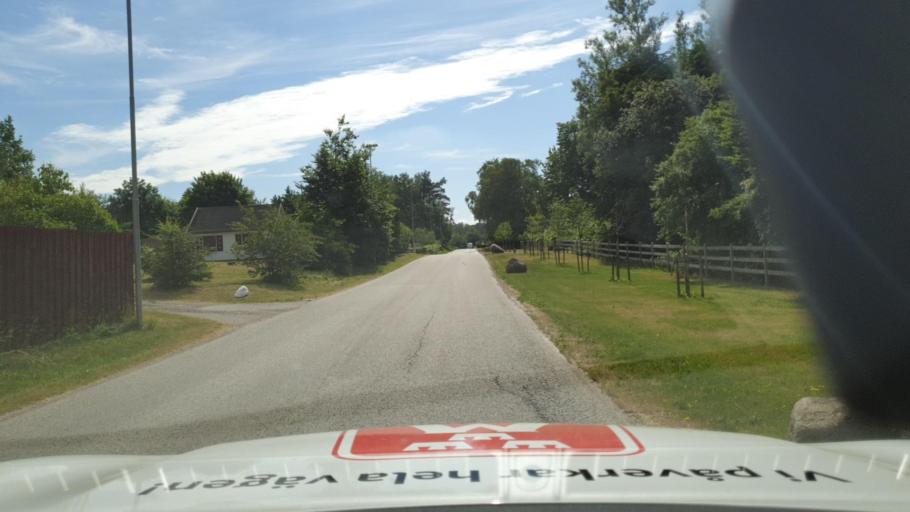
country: SE
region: Skane
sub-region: Sjobo Kommun
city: Sjoebo
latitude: 55.6308
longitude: 13.7278
